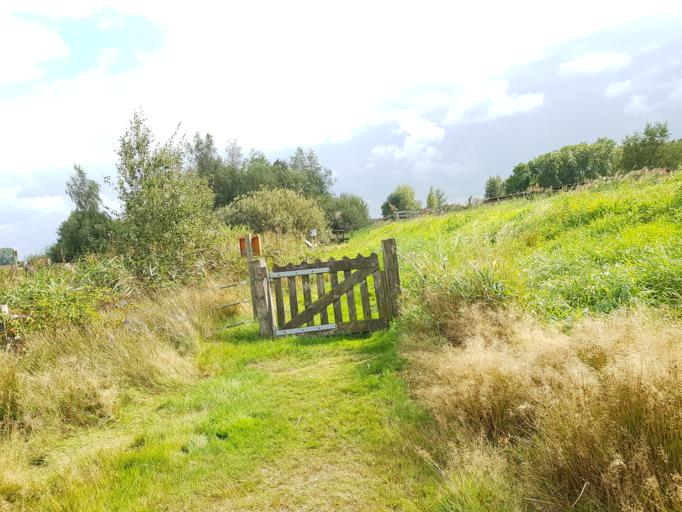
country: NL
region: Groningen
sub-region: Gemeente Slochteren
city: Slochteren
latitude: 53.2288
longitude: 6.7427
